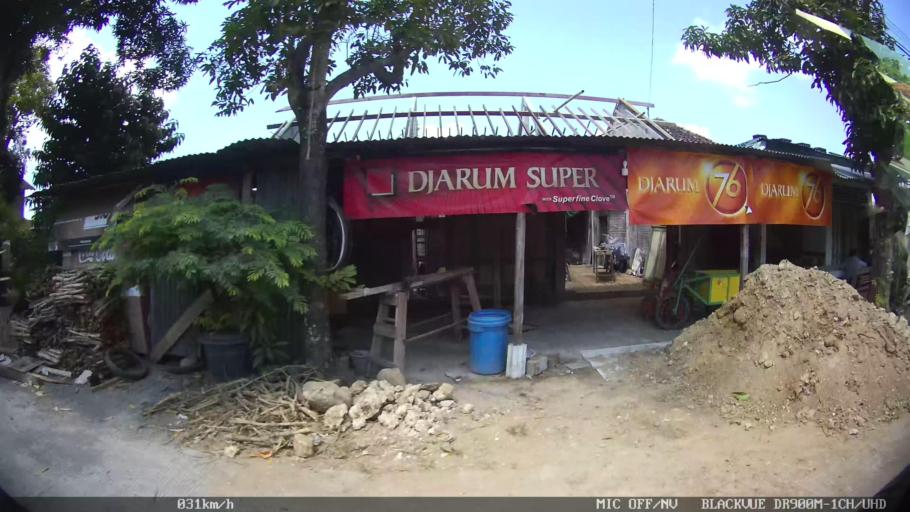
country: ID
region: Daerah Istimewa Yogyakarta
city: Pundong
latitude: -7.9253
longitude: 110.3735
